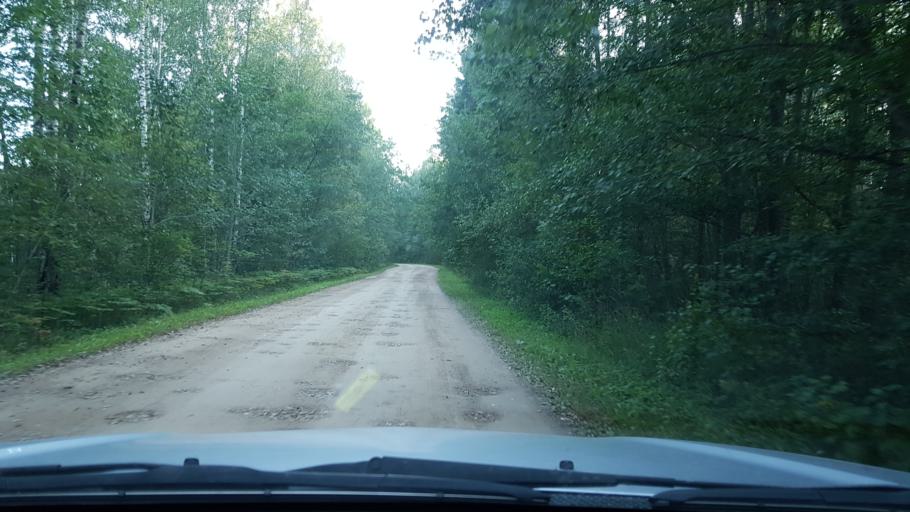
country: EE
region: Ida-Virumaa
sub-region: Sillamaee linn
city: Sillamae
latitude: 59.2638
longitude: 27.9218
